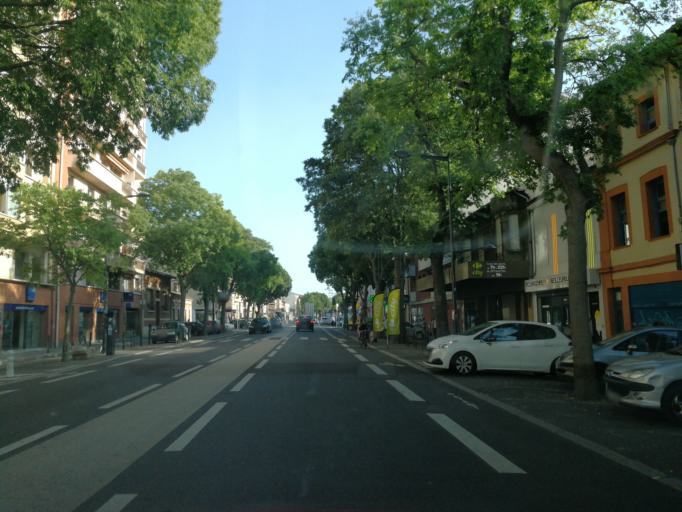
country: FR
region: Midi-Pyrenees
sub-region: Departement de la Haute-Garonne
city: Toulouse
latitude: 43.6218
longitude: 1.4351
